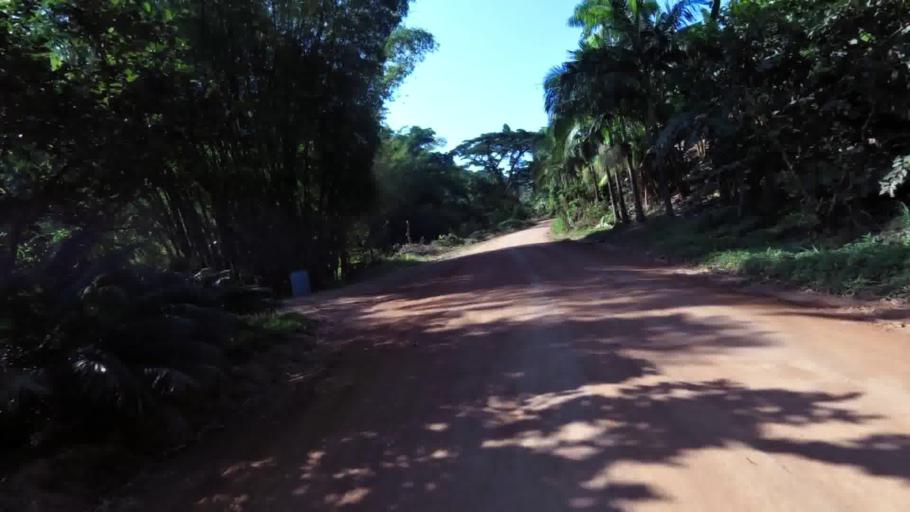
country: BR
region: Espirito Santo
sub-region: Alfredo Chaves
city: Alfredo Chaves
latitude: -20.5542
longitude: -40.7272
